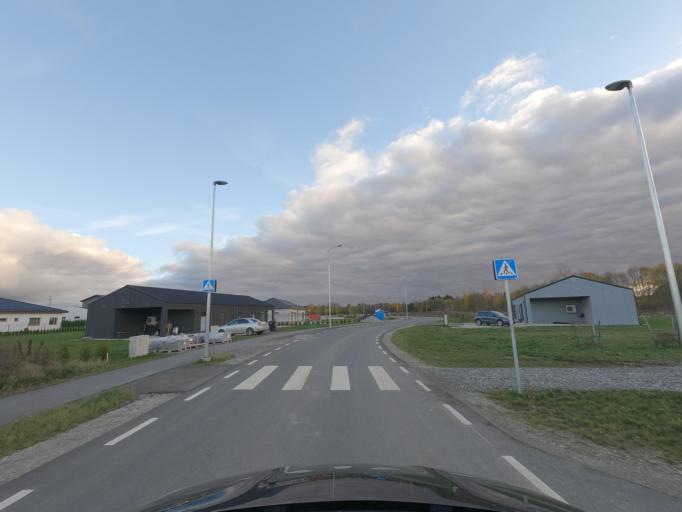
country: EE
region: Harju
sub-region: Saue vald
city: Laagri
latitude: 59.3622
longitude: 24.5724
